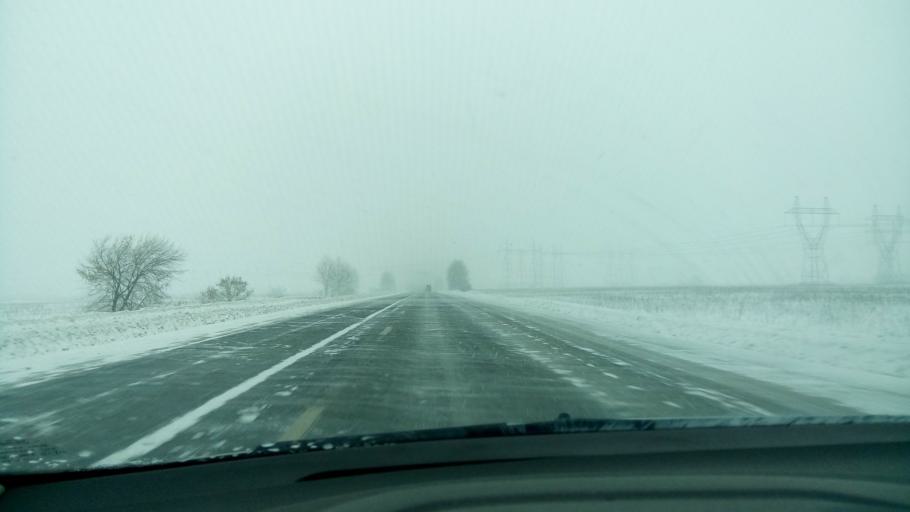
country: RU
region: Sverdlovsk
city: Beloyarskiy
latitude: 56.7736
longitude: 61.5091
